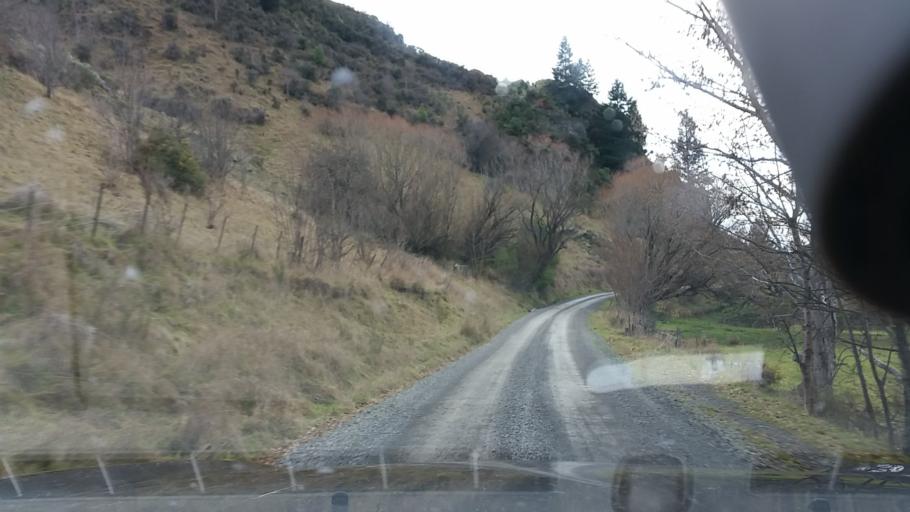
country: NZ
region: Tasman
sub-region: Tasman District
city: Richmond
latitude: -41.7216
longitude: 173.4701
